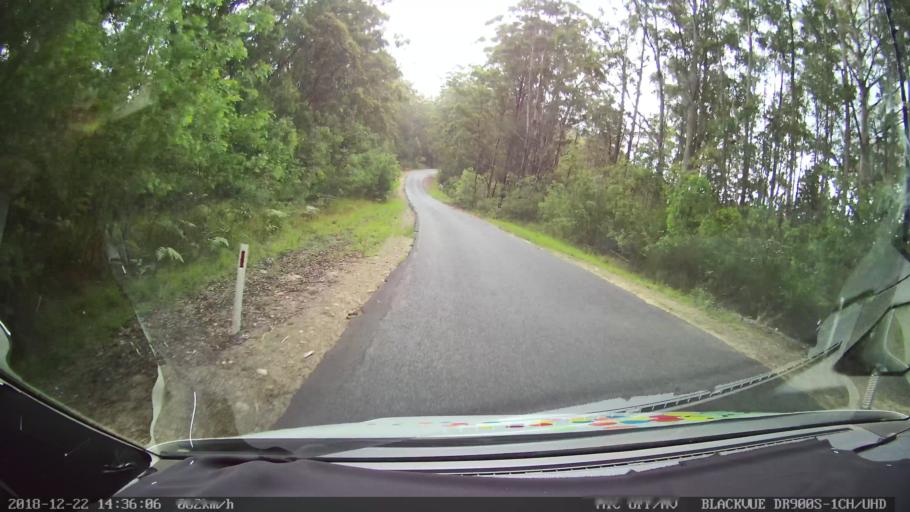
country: AU
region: New South Wales
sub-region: Bellingen
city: Dorrigo
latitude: -30.1263
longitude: 152.6084
